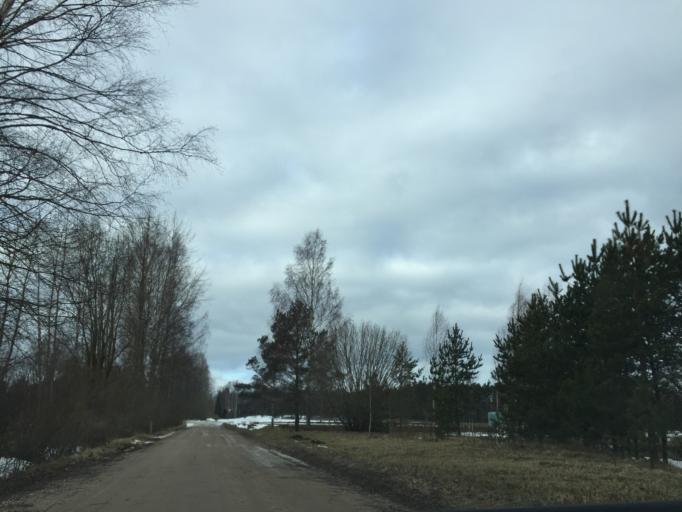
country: LV
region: Salacgrivas
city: Ainazi
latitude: 57.8484
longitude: 24.4860
